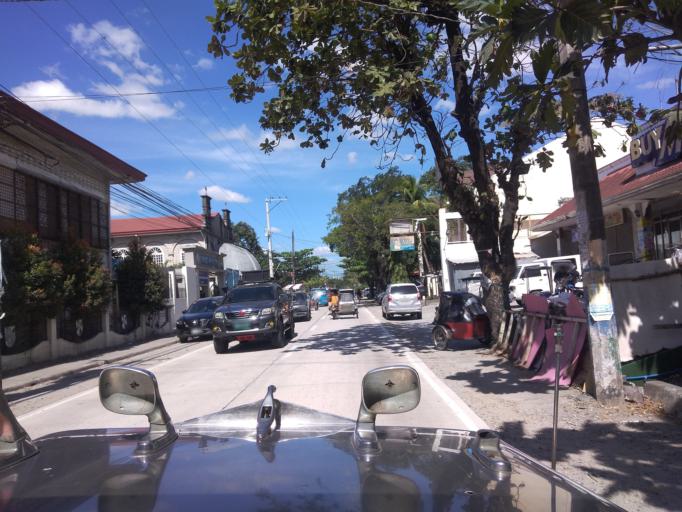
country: PH
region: Central Luzon
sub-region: Province of Pampanga
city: Santa Rita
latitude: 14.9993
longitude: 120.6123
